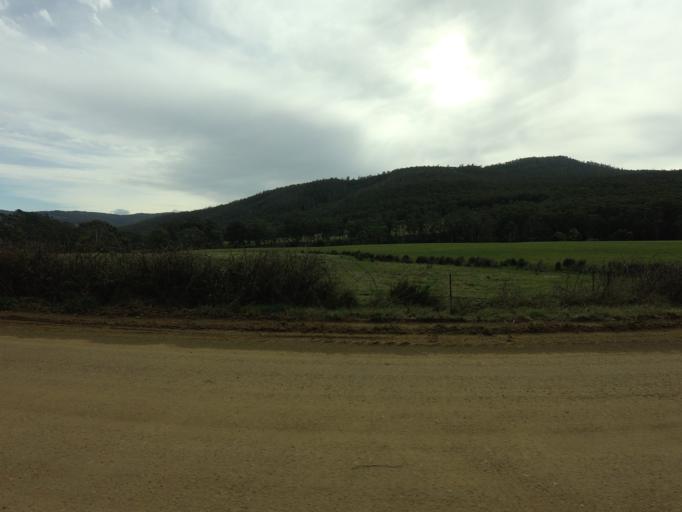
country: AU
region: Tasmania
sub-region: Huon Valley
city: Huonville
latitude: -43.0759
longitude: 147.0631
